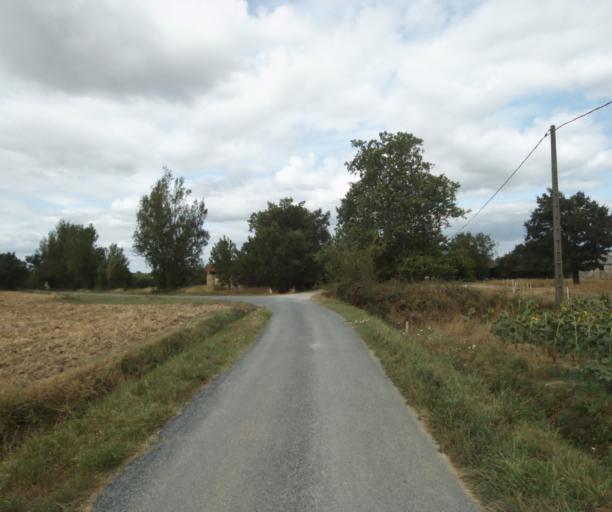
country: FR
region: Midi-Pyrenees
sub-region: Departement du Tarn
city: Soreze
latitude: 43.4719
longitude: 2.0415
